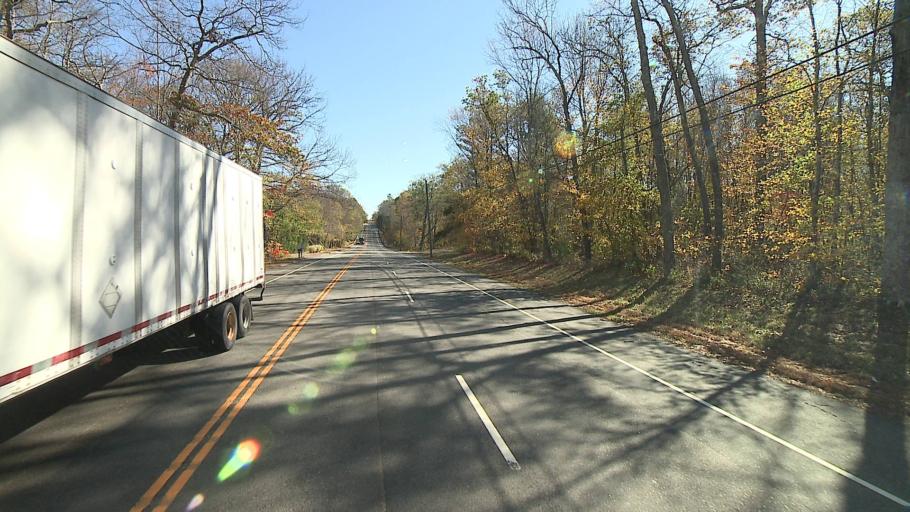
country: US
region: Connecticut
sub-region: Windham County
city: South Woodstock
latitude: 41.8743
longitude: -72.0697
